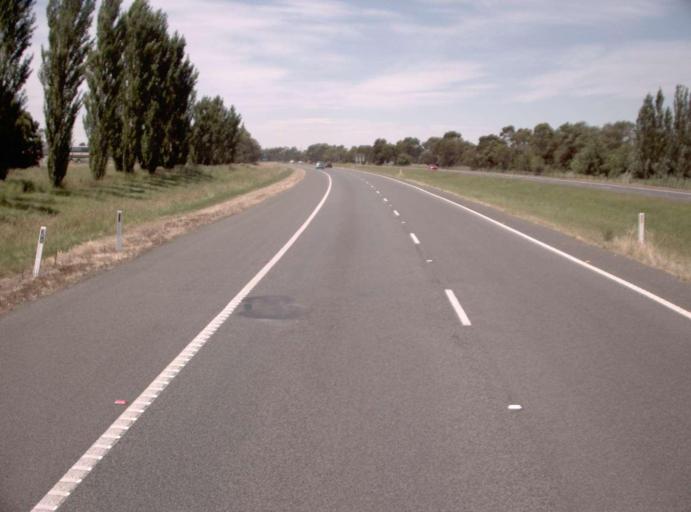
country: AU
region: Victoria
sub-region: Latrobe
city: Morwell
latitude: -38.2449
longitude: 146.4372
